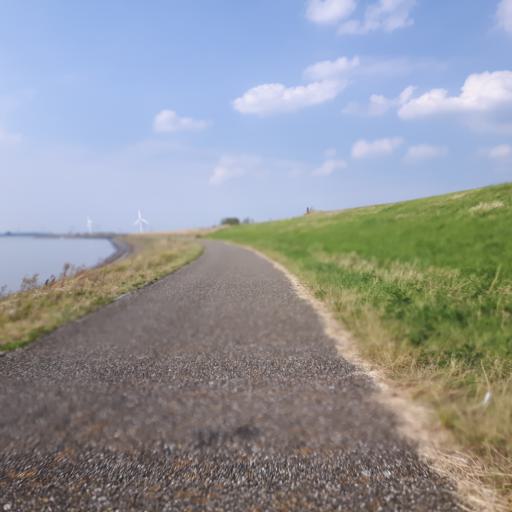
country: NL
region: Zeeland
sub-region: Gemeente Reimerswaal
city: Yerseke
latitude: 51.4483
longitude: 3.9982
